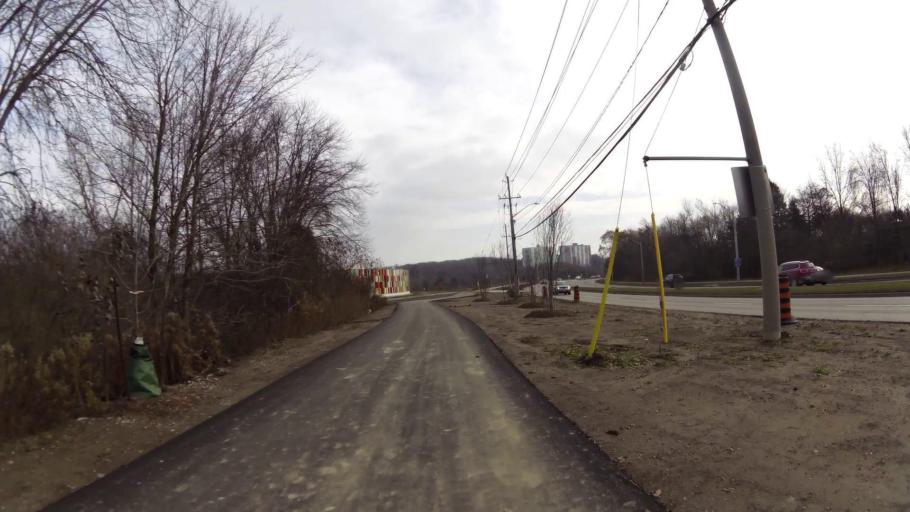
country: CA
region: Ontario
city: Kitchener
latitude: 43.4001
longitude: -80.4405
